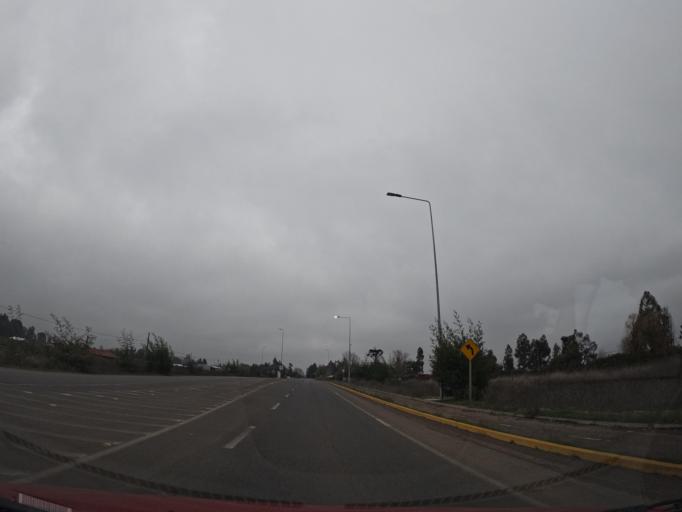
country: CL
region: Maule
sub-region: Provincia de Talca
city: San Clemente
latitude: -35.5474
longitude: -71.4715
